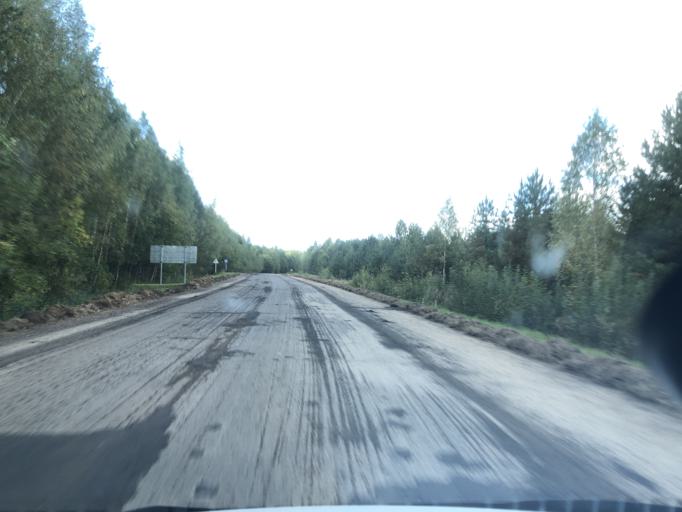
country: RU
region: Jaroslavl
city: Porech'ye-Rybnoye
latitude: 56.9651
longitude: 39.4554
